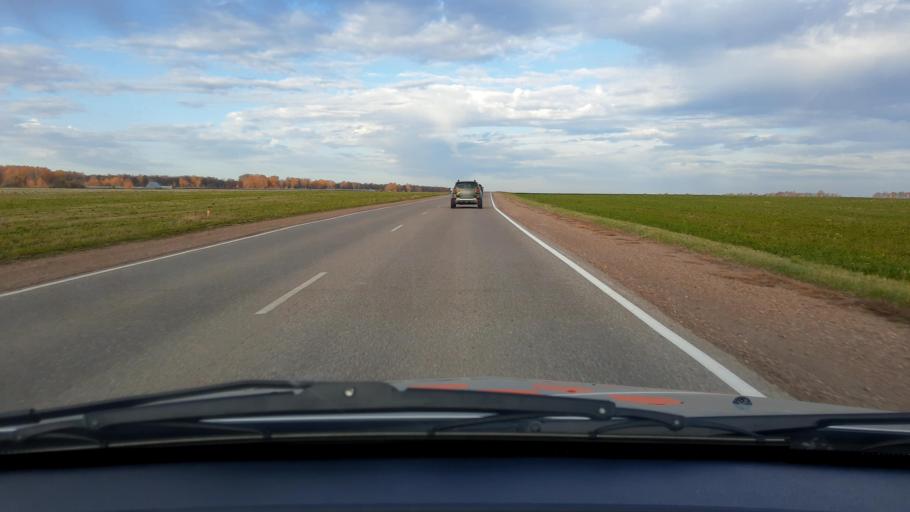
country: RU
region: Bashkortostan
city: Avdon
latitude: 54.8222
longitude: 55.6635
